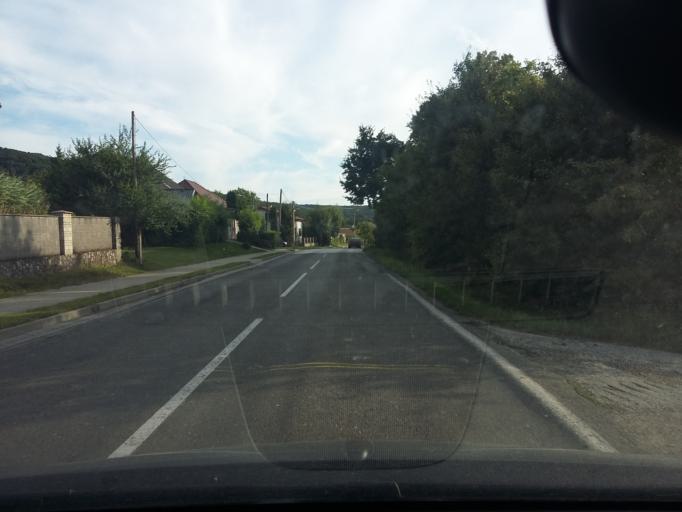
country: SK
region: Bratislavsky
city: Svaty Jur
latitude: 48.3713
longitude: 17.1473
